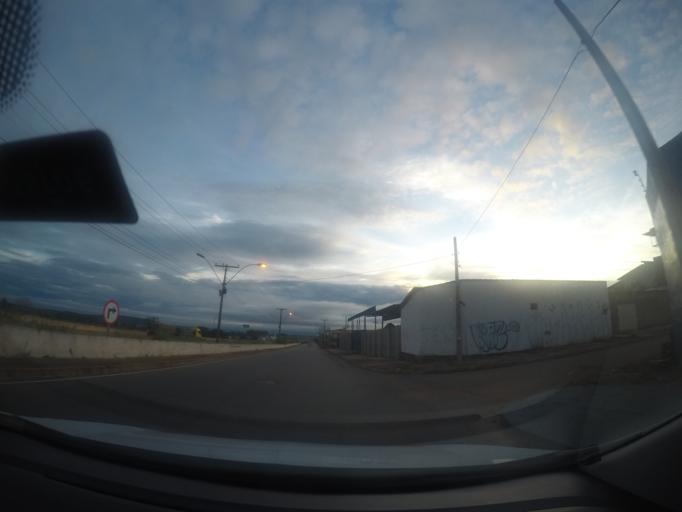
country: BR
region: Goias
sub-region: Goiania
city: Goiania
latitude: -16.7204
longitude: -49.3704
